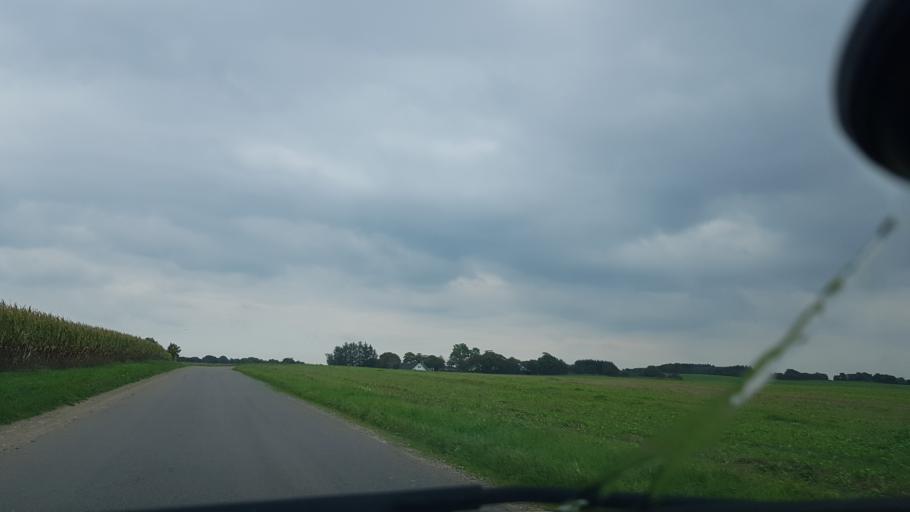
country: DK
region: South Denmark
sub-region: Vejle Kommune
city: Egtved
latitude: 55.5569
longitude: 9.3263
